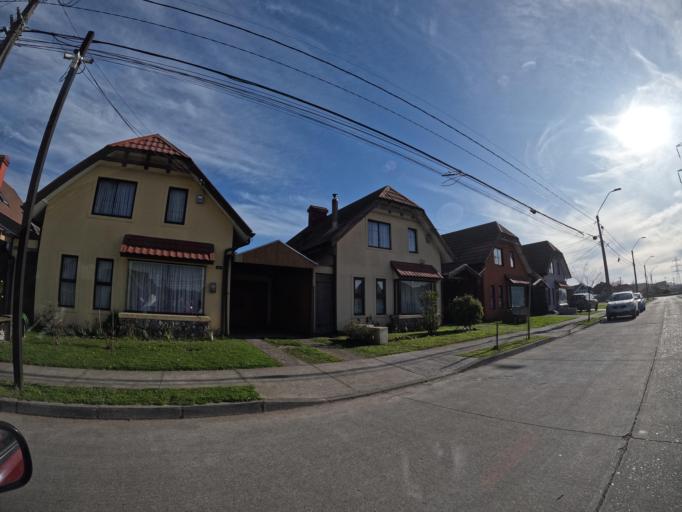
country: CL
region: Biobio
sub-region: Provincia de Concepcion
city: Talcahuano
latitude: -36.7723
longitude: -73.0782
